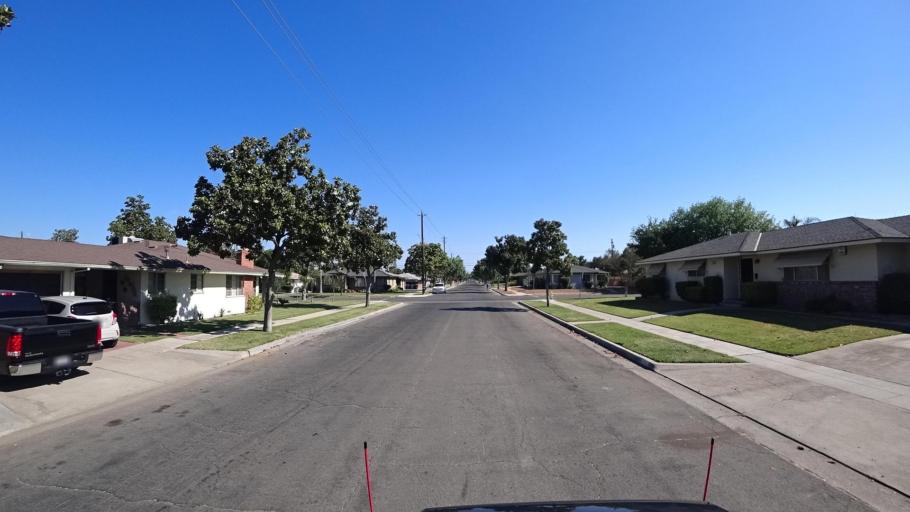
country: US
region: California
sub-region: Fresno County
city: Fresno
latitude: 36.7744
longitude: -119.8221
